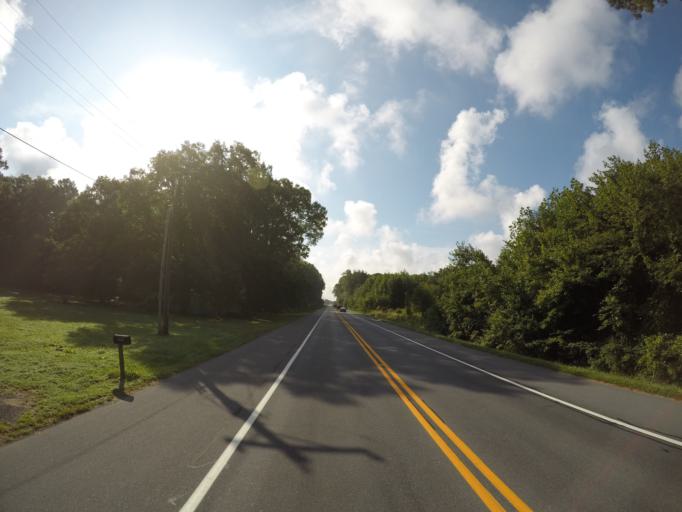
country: US
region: Delaware
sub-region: Sussex County
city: Bridgeville
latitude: 38.7635
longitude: -75.6424
